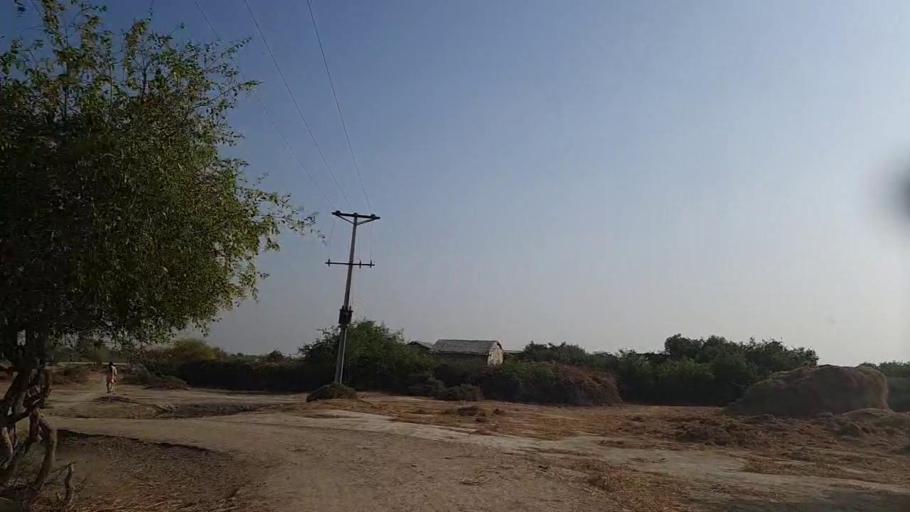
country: PK
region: Sindh
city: Jati
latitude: 24.5226
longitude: 68.2681
